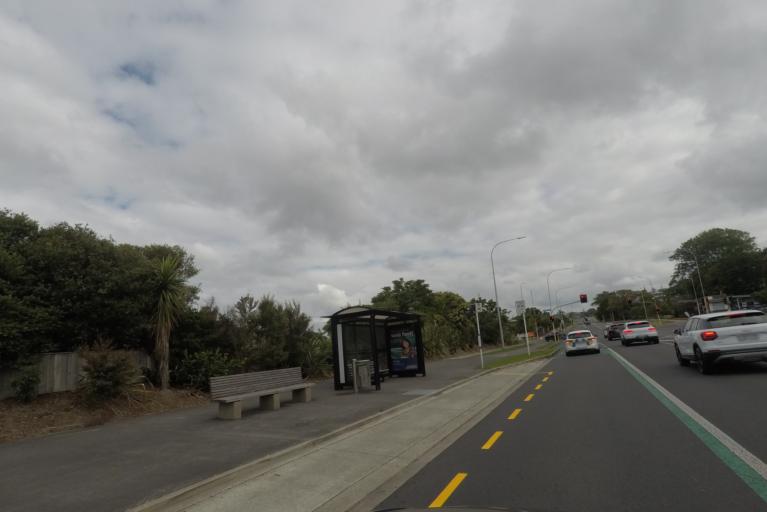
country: NZ
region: Auckland
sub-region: Auckland
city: Rothesay Bay
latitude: -36.7421
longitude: 174.6928
